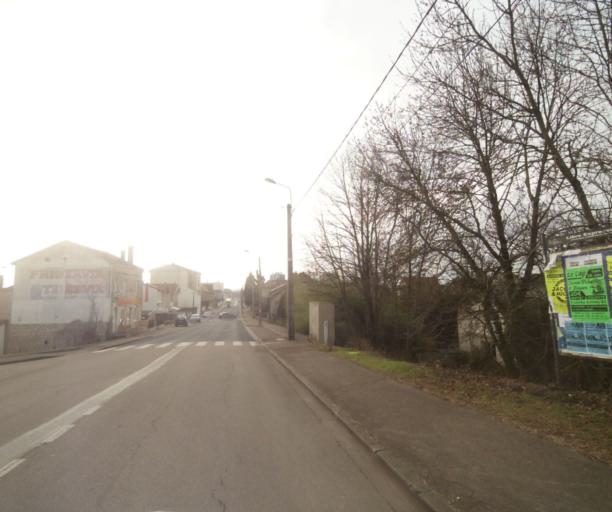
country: FR
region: Champagne-Ardenne
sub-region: Departement de la Haute-Marne
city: Saint-Dizier
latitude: 48.6421
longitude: 4.9332
